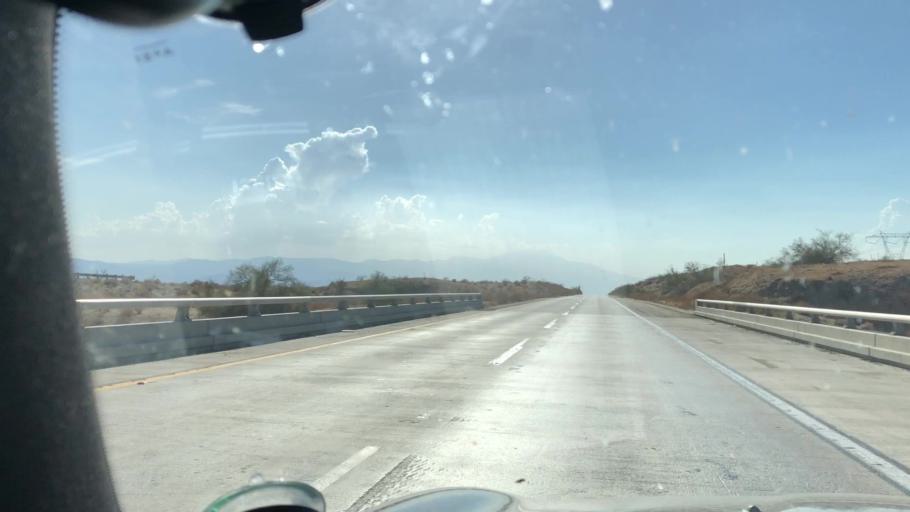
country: US
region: California
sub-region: Riverside County
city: Thermal
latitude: 33.6870
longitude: -116.0285
